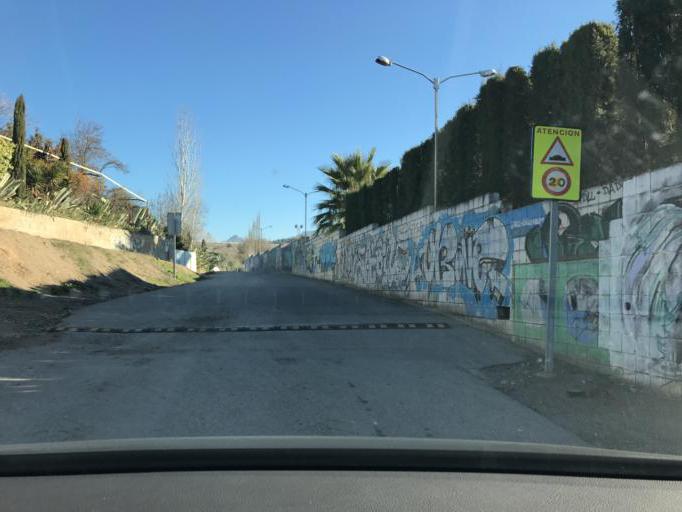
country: ES
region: Andalusia
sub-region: Provincia de Granada
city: Peligros
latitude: 37.2374
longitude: -3.6198
